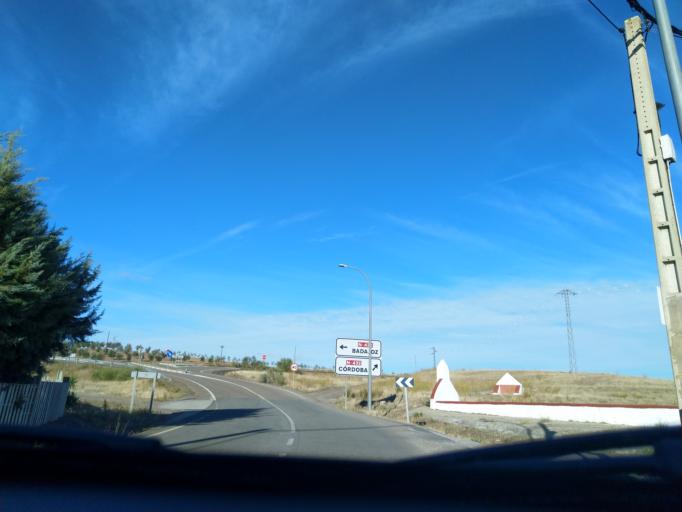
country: ES
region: Extremadura
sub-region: Provincia de Badajoz
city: Ahillones
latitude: 38.2630
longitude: -5.8613
